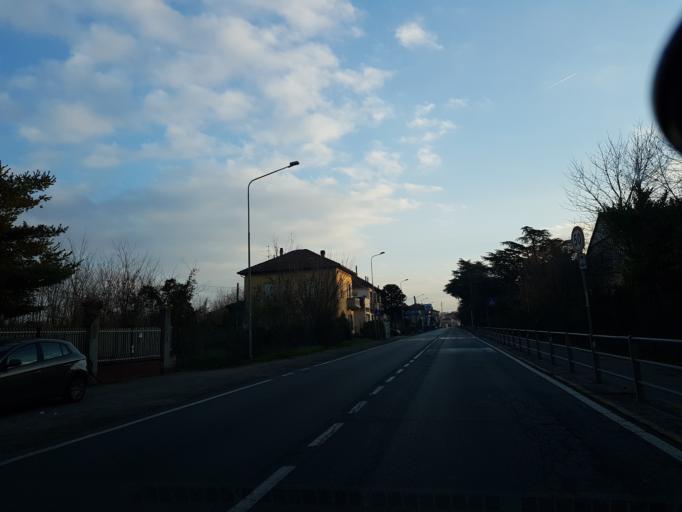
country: IT
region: Piedmont
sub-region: Provincia di Alessandria
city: Novi Ligure
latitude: 44.7771
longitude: 8.7895
